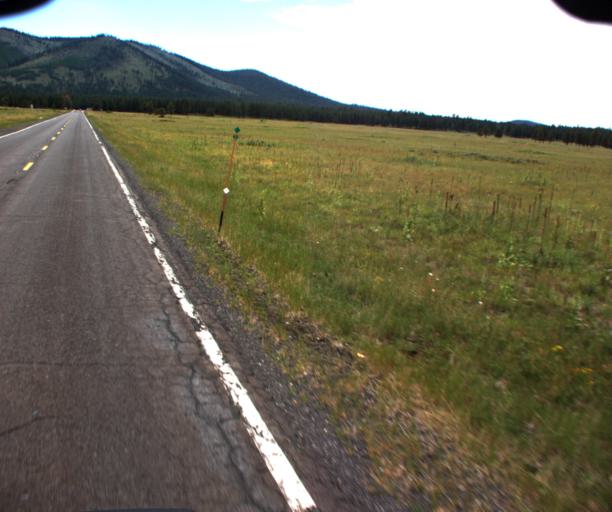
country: US
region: Arizona
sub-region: Coconino County
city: Flagstaff
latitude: 35.4095
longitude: -111.7556
